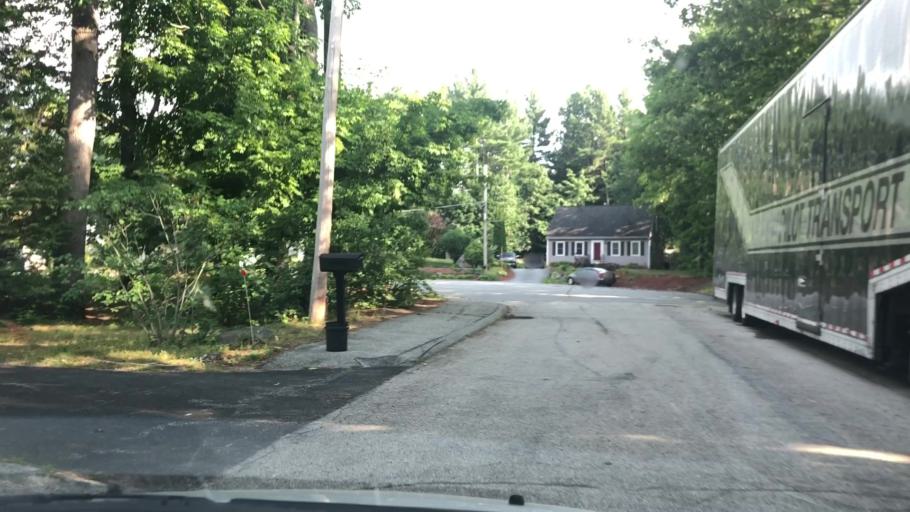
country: US
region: New Hampshire
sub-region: Hillsborough County
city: Milford
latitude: 42.8286
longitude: -71.6450
